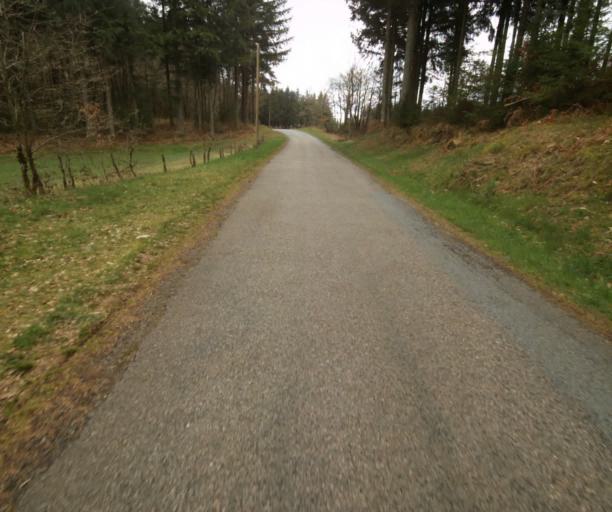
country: FR
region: Limousin
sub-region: Departement de la Correze
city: Correze
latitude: 45.3238
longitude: 1.9167
